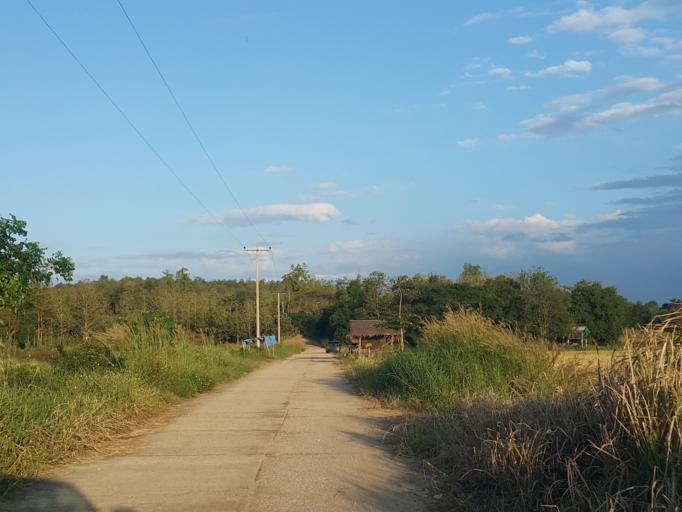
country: TH
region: Lampang
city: Mae Mo
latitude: 18.4348
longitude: 99.5897
